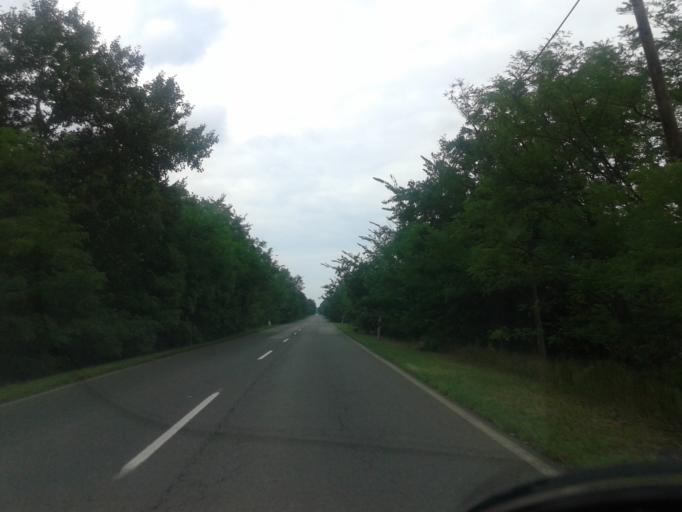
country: HU
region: Csongrad
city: Asotthalom
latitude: 46.2174
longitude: 19.7790
